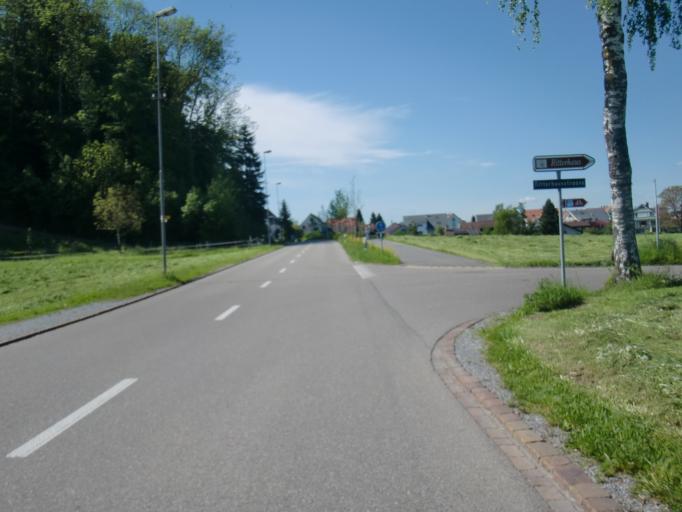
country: CH
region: Zurich
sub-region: Bezirk Hinwil
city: Bubikon
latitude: 47.2653
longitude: 8.8234
